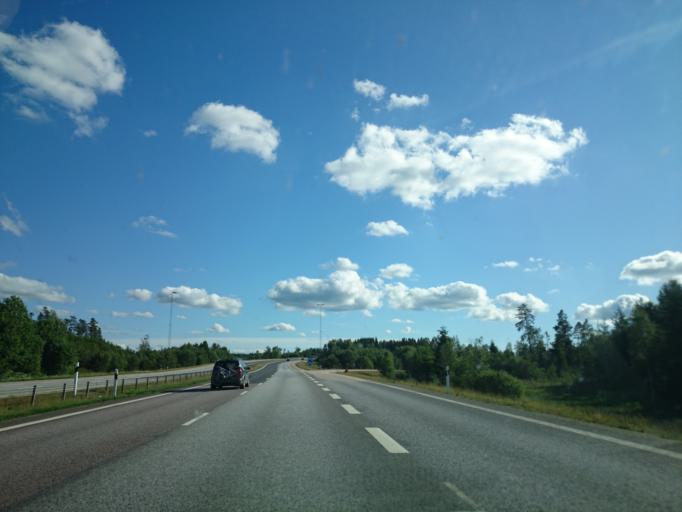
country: SE
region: Kronoberg
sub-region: Markaryds Kommun
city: Stromsnasbruk
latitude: 56.6267
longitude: 13.7862
